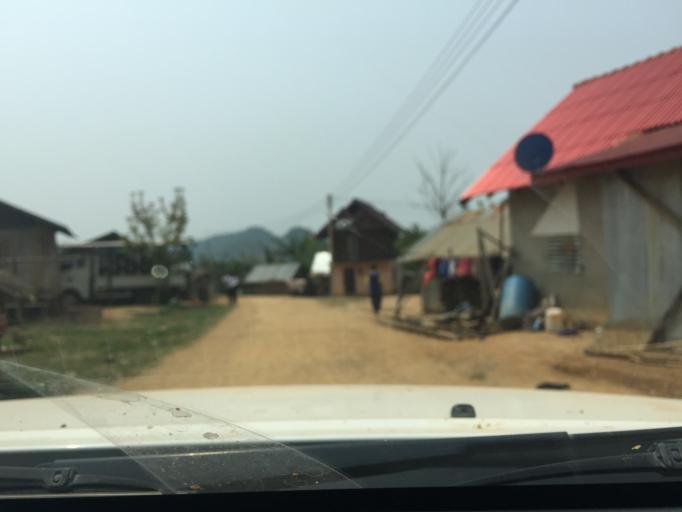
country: LA
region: Loungnamtha
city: Muang Nale
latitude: 20.6326
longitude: 101.6500
